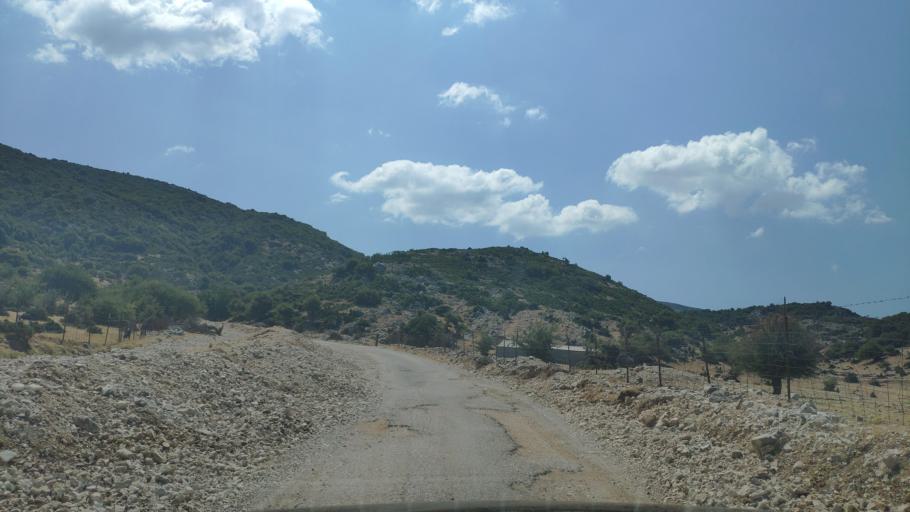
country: GR
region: West Greece
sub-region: Nomos Aitolias kai Akarnanias
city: Monastirakion
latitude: 38.8070
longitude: 20.9432
